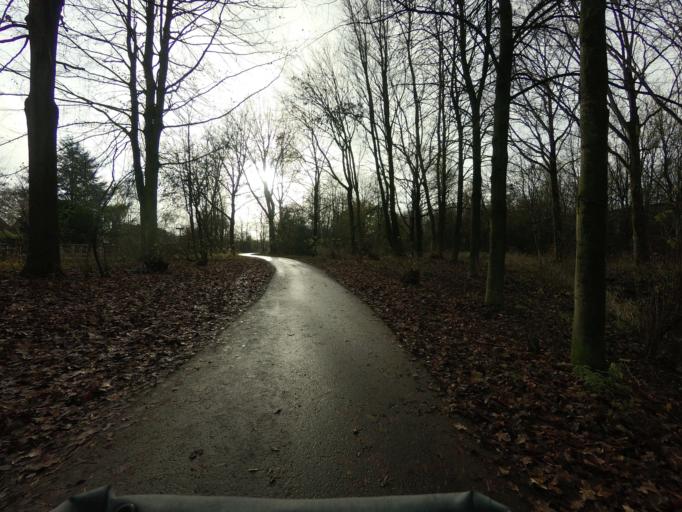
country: NL
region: Utrecht
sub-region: Gemeente Nieuwegein
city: Nieuwegein
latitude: 52.0355
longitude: 5.0657
